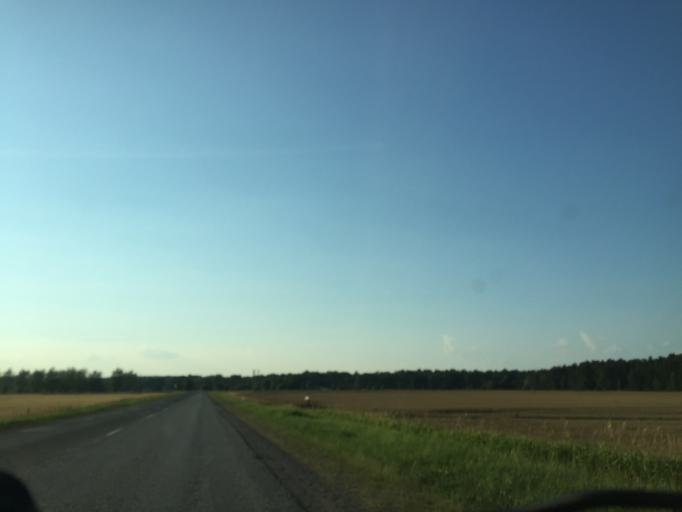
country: LV
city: Tervete
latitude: 56.4726
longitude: 23.3969
